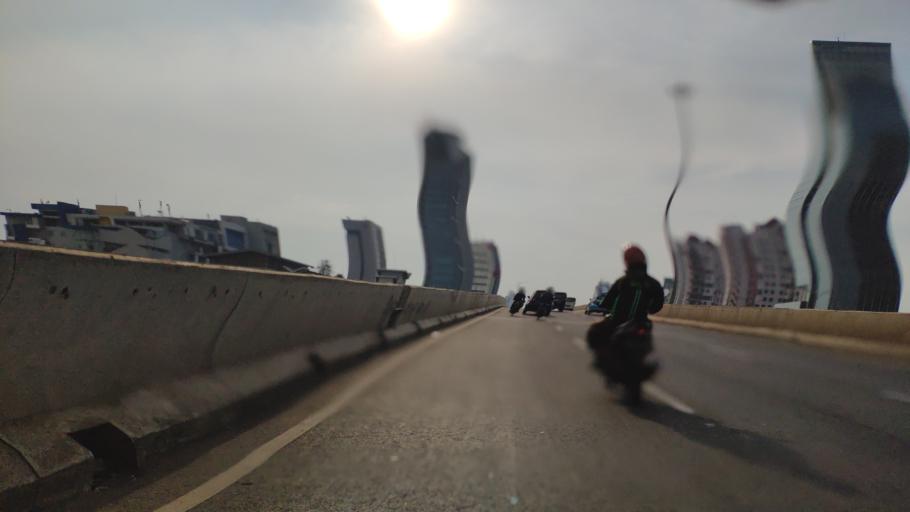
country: ID
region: West Java
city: Pamulang
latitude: -6.2928
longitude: 106.8063
